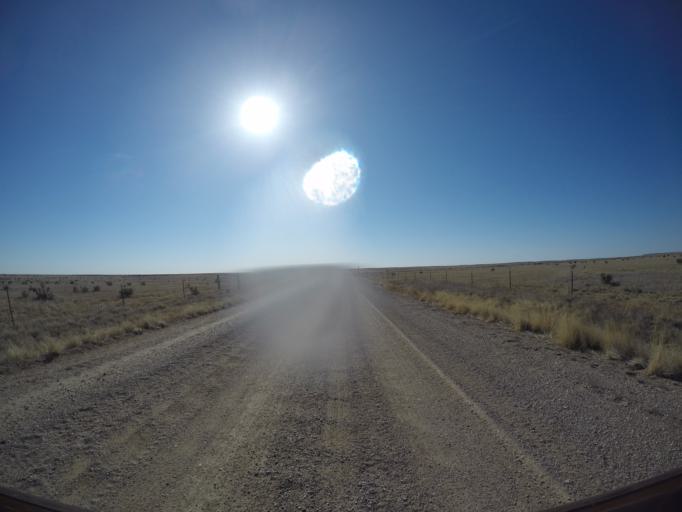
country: US
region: Colorado
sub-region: Otero County
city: La Junta
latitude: 37.7064
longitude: -103.6204
